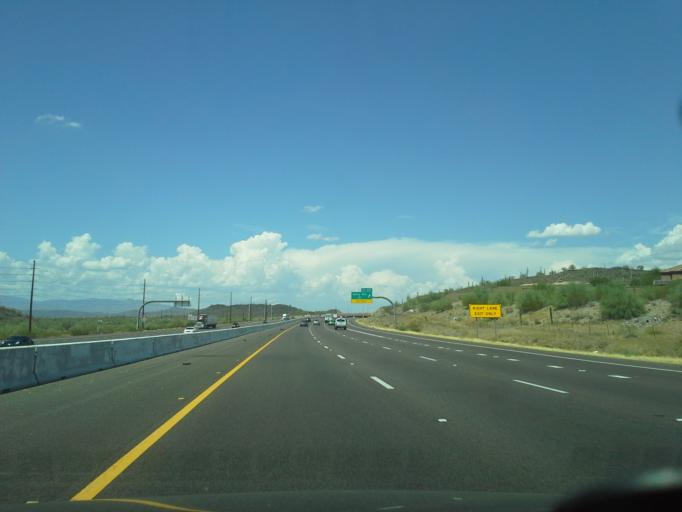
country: US
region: Arizona
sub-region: Maricopa County
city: Anthem
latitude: 33.8325
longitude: -112.1448
